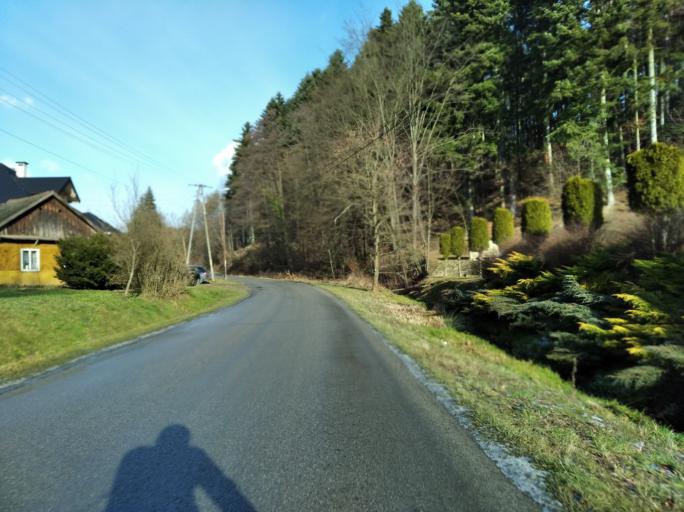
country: PL
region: Subcarpathian Voivodeship
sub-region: Powiat strzyzowski
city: Strzyzow
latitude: 49.8924
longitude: 21.7777
